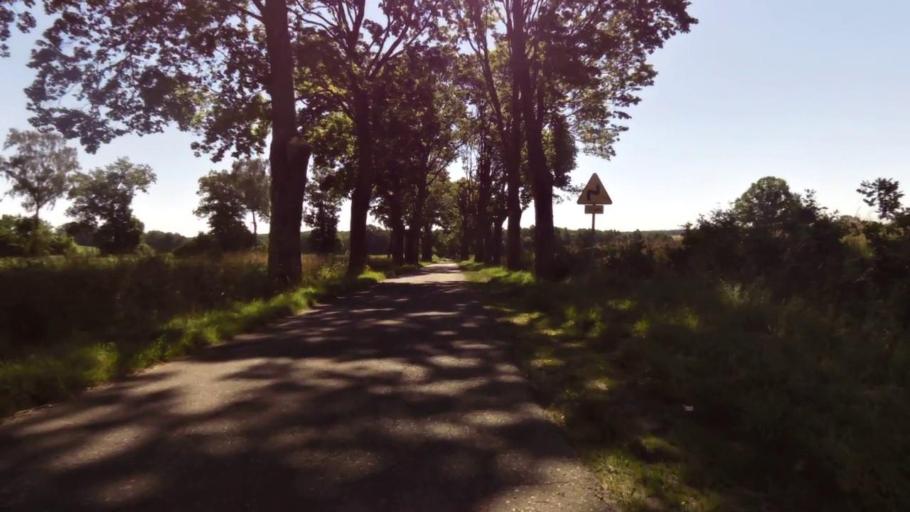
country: PL
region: West Pomeranian Voivodeship
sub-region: Powiat bialogardzki
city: Bialogard
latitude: 53.9377
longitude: 15.9870
